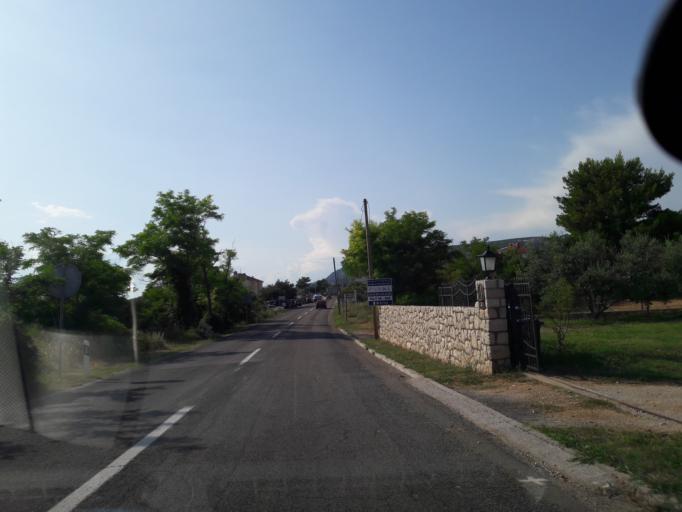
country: HR
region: Primorsko-Goranska
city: Banjol
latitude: 44.7248
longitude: 14.8188
